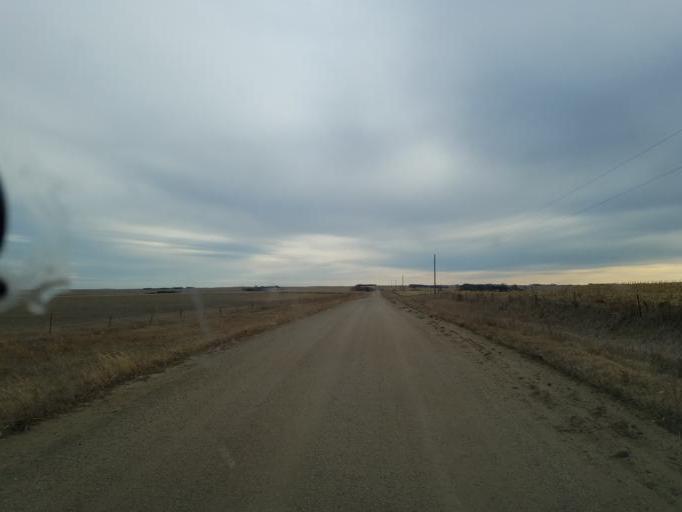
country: US
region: Nebraska
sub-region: Knox County
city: Bloomfield
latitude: 42.5251
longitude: -97.7336
